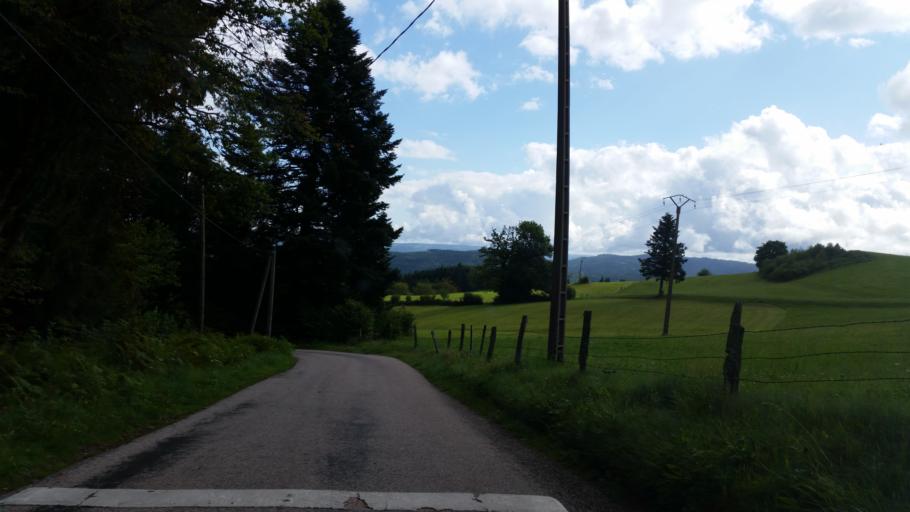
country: FR
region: Lorraine
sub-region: Departement des Vosges
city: Vecoux
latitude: 47.9690
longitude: 6.6025
